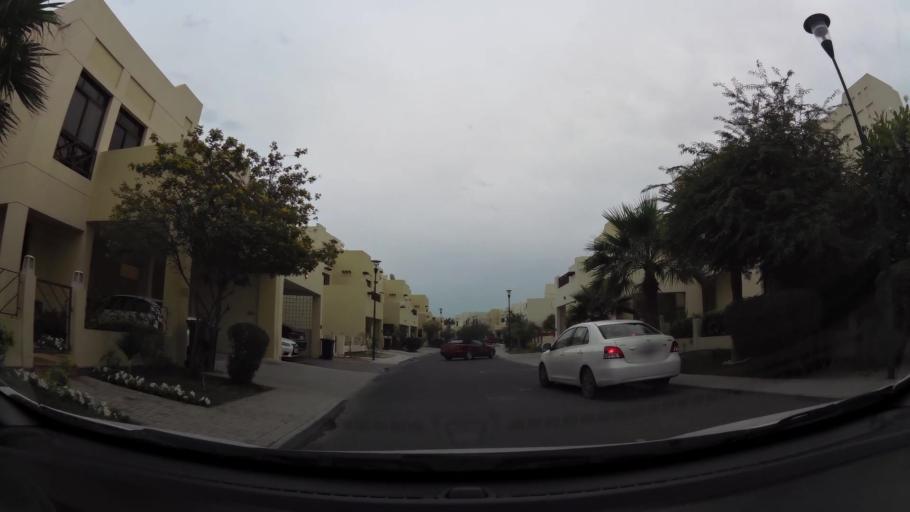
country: BH
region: Northern
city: Ar Rifa'
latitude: 26.1014
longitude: 50.5691
